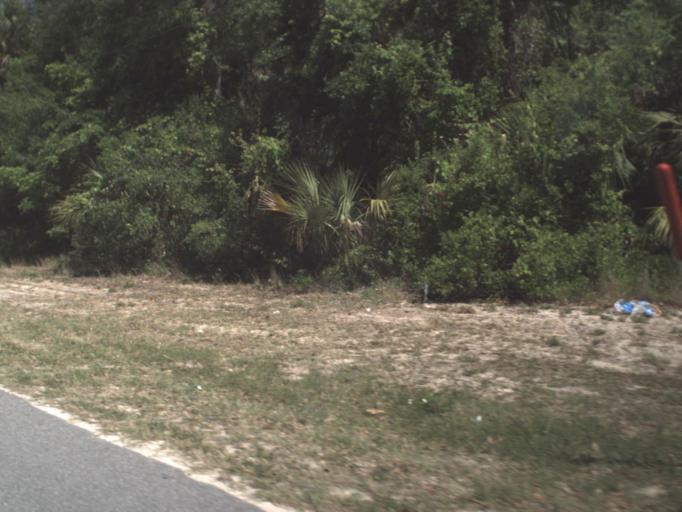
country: US
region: Florida
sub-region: Flagler County
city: Palm Coast
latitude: 29.6091
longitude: -81.2004
